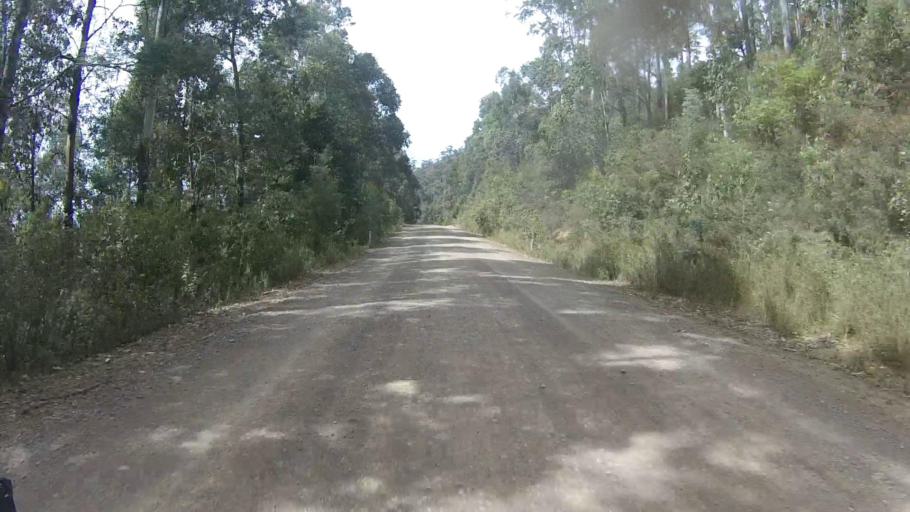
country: AU
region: Tasmania
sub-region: Sorell
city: Sorell
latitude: -42.7621
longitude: 147.8298
